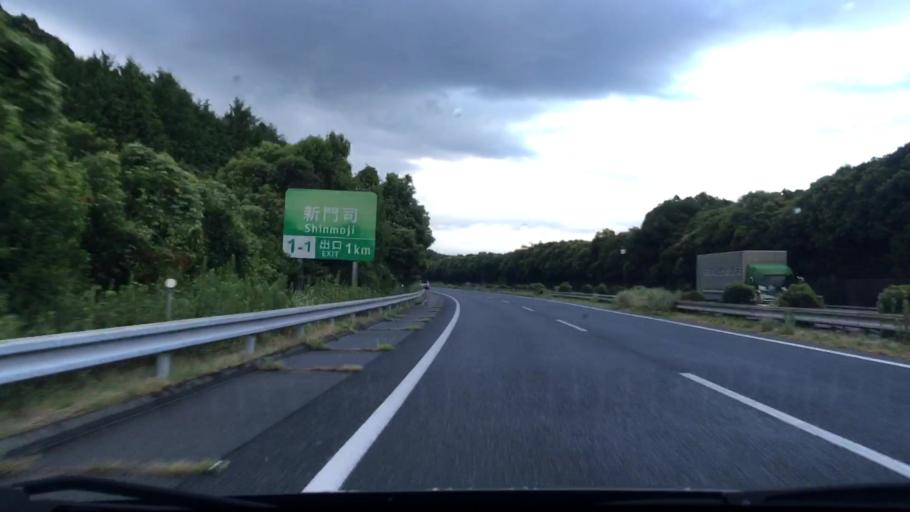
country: JP
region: Yamaguchi
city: Shimonoseki
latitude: 33.8764
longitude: 130.9688
